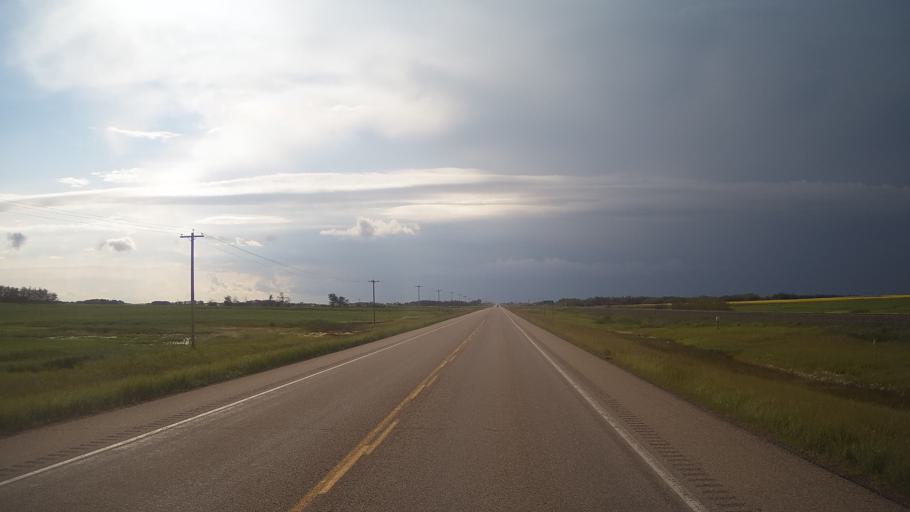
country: CA
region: Alberta
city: Viking
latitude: 53.1806
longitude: -112.0704
